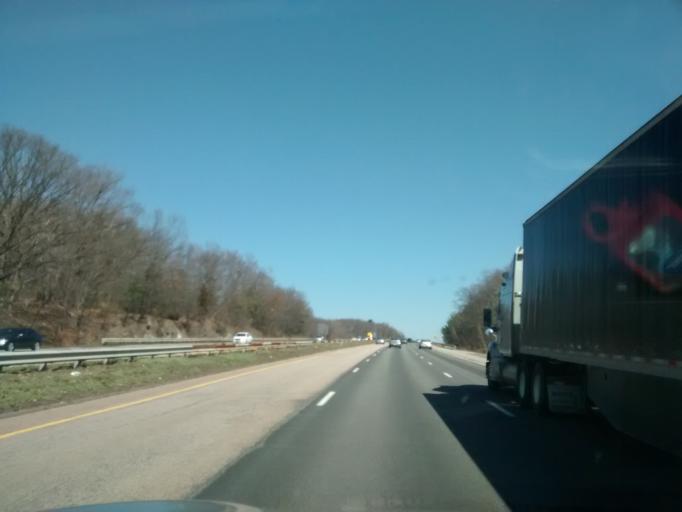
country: US
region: Massachusetts
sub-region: Worcester County
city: Millbury
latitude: 42.2217
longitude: -71.7519
